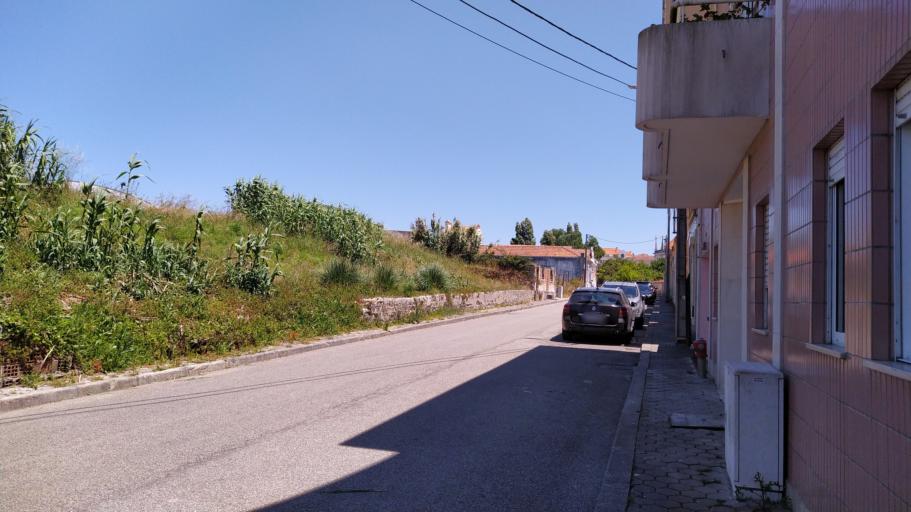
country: PT
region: Aveiro
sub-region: Aveiro
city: Aveiro
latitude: 40.6487
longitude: -8.6436
